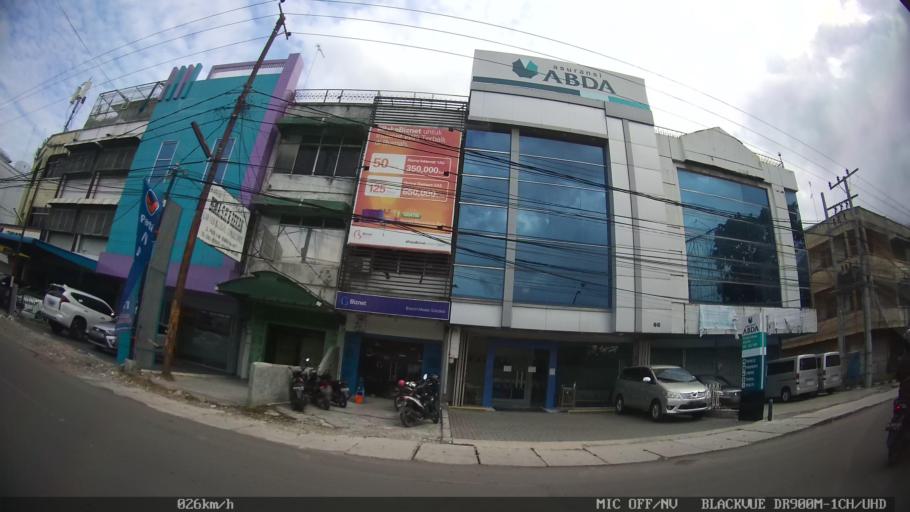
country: ID
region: North Sumatra
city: Medan
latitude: 3.5957
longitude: 98.6843
